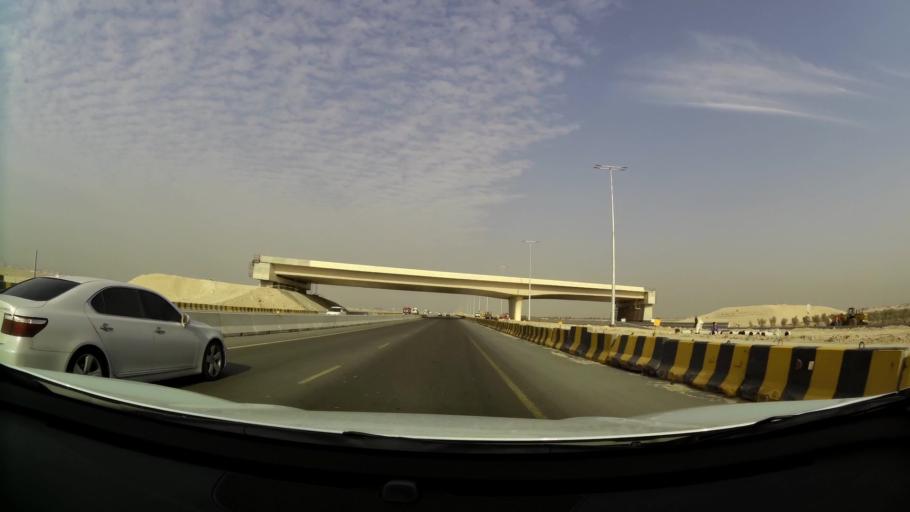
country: AE
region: Abu Dhabi
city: Abu Dhabi
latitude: 24.2778
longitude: 54.5229
